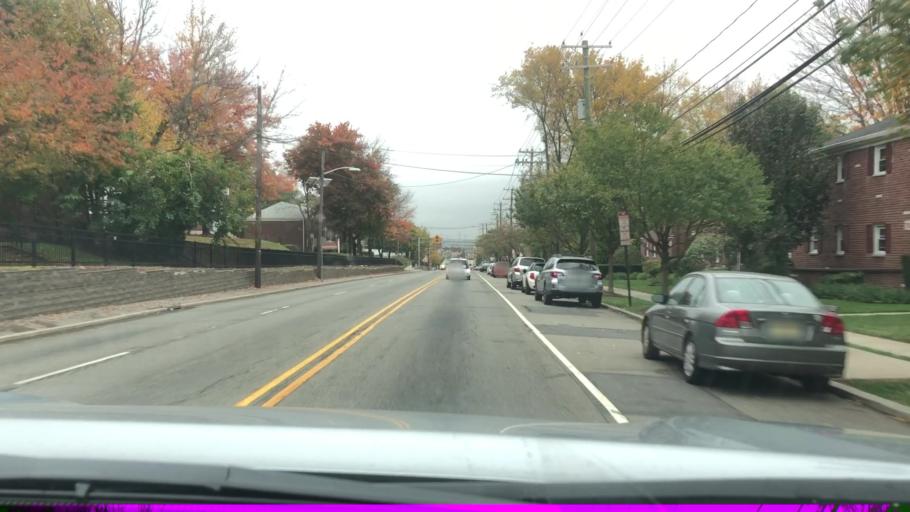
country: US
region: New Jersey
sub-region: Bergen County
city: Ridgefield
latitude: 40.8376
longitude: -74.0060
